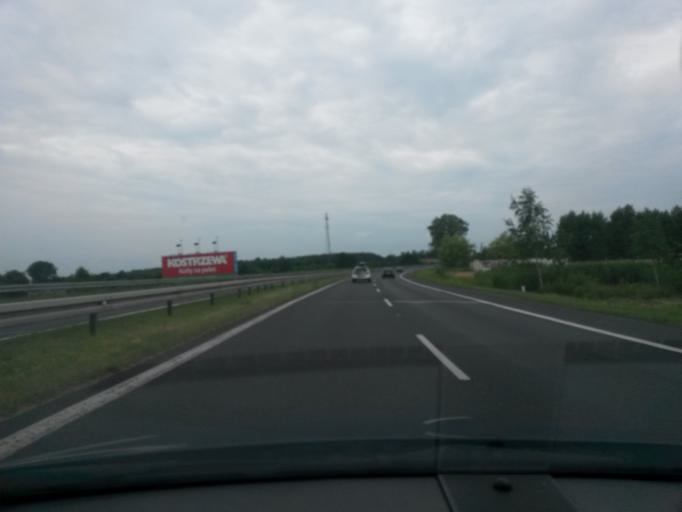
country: PL
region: Masovian Voivodeship
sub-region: Powiat zyrardowski
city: Radziejowice
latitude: 52.0056
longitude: 20.6011
